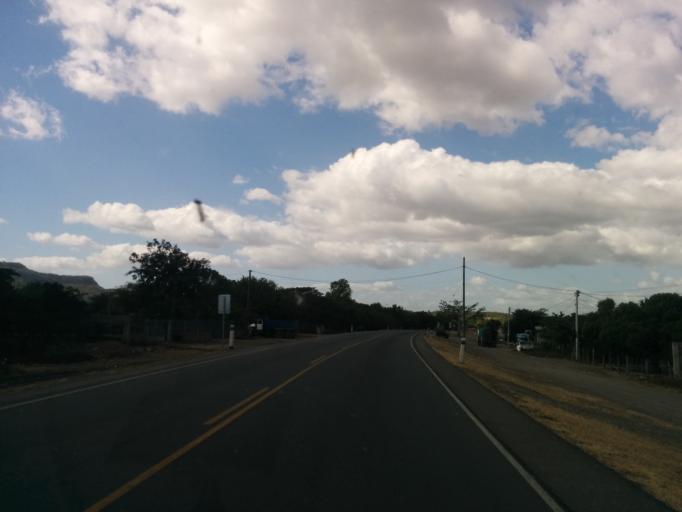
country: NI
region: Matagalpa
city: Ciudad Dario
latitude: 12.6633
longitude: -86.0856
